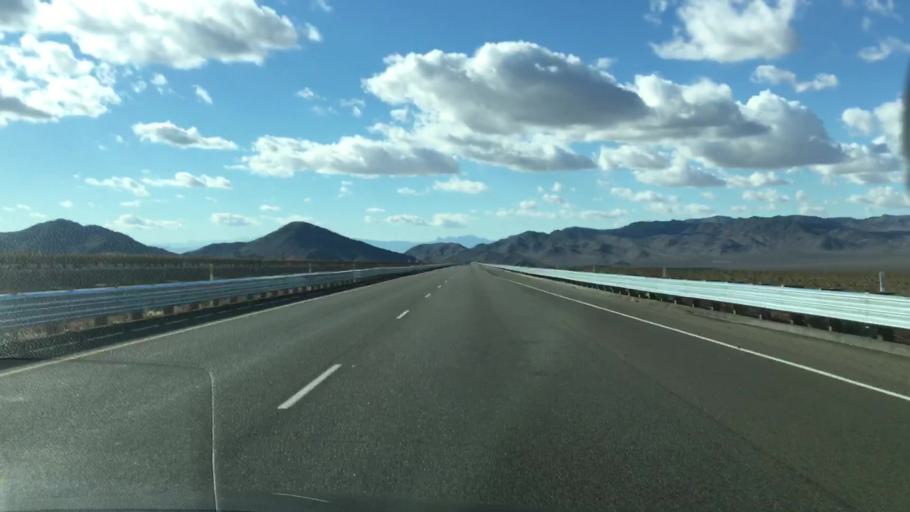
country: US
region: Nevada
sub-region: Nye County
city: Pahrump
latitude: 36.5971
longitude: -116.0038
